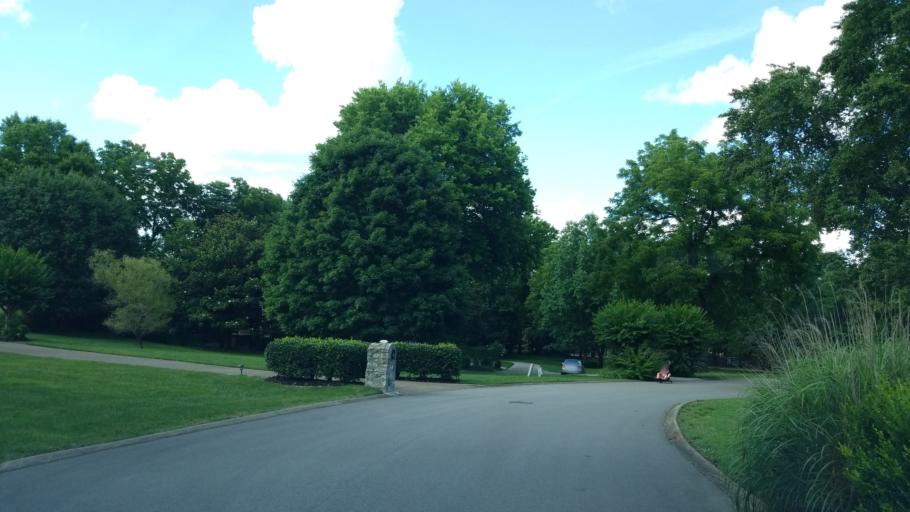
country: US
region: Tennessee
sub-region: Davidson County
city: Forest Hills
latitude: 36.0269
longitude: -86.8335
